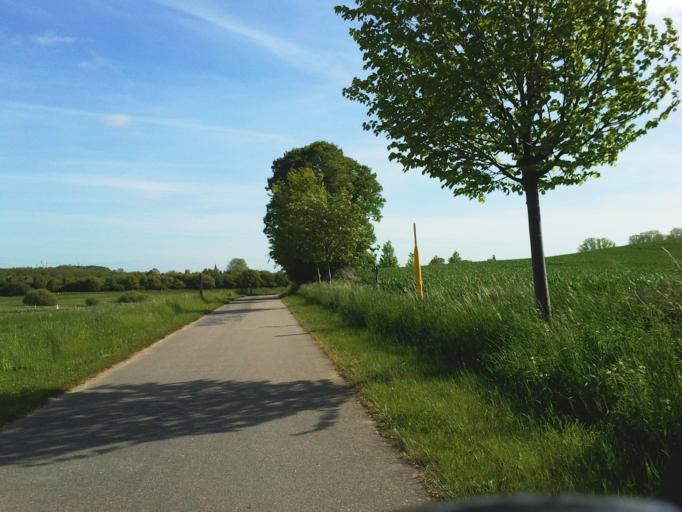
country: DE
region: Mecklenburg-Vorpommern
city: Schwaan
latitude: 53.9543
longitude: 12.1050
